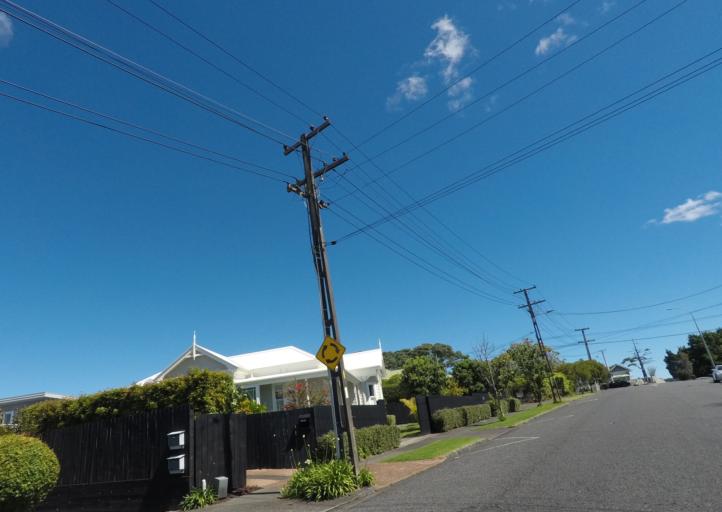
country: NZ
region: Auckland
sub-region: Auckland
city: Auckland
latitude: -36.8728
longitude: 174.7325
